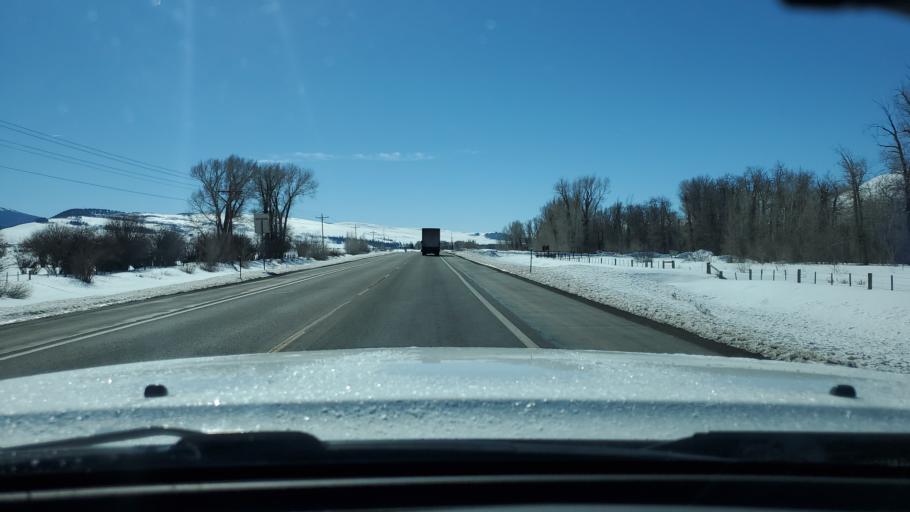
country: US
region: Colorado
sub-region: Gunnison County
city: Crested Butte
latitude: 38.7612
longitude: -106.8632
